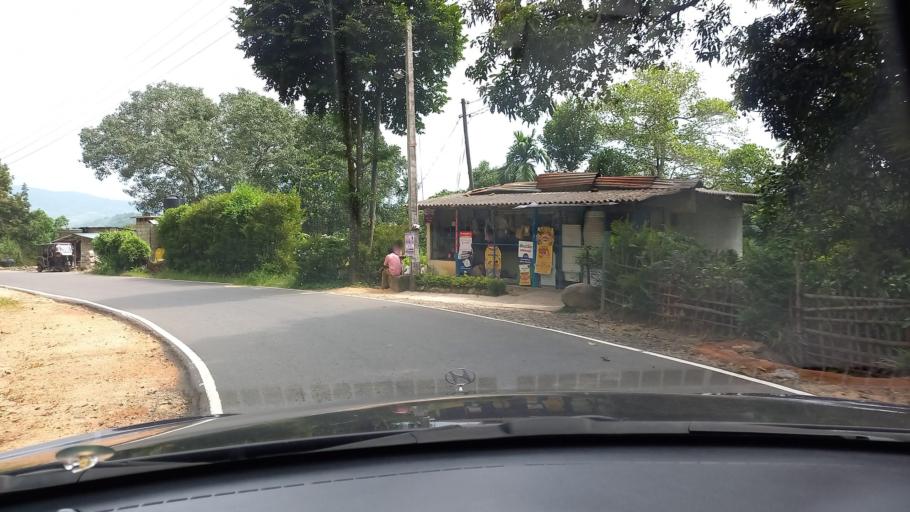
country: LK
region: Central
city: Gampola
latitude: 7.2246
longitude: 80.6065
